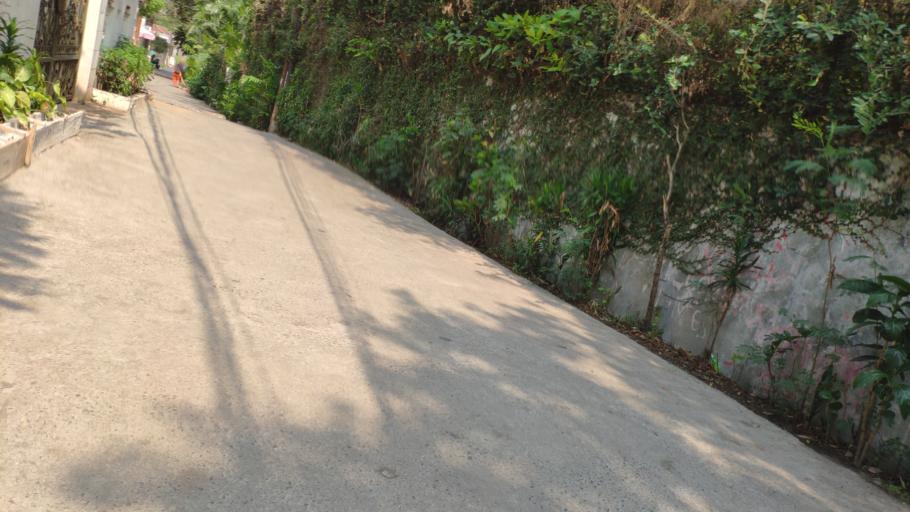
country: ID
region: Jakarta Raya
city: Jakarta
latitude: -6.2549
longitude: 106.8118
